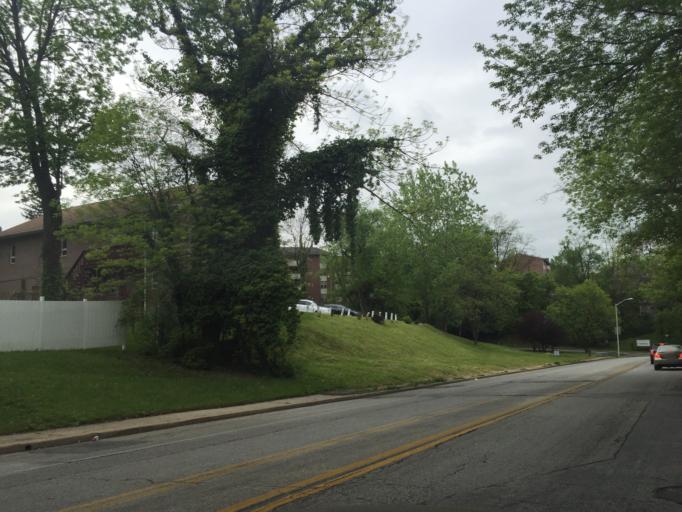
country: US
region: Maryland
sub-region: Baltimore County
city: Lochearn
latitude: 39.3382
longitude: -76.6569
